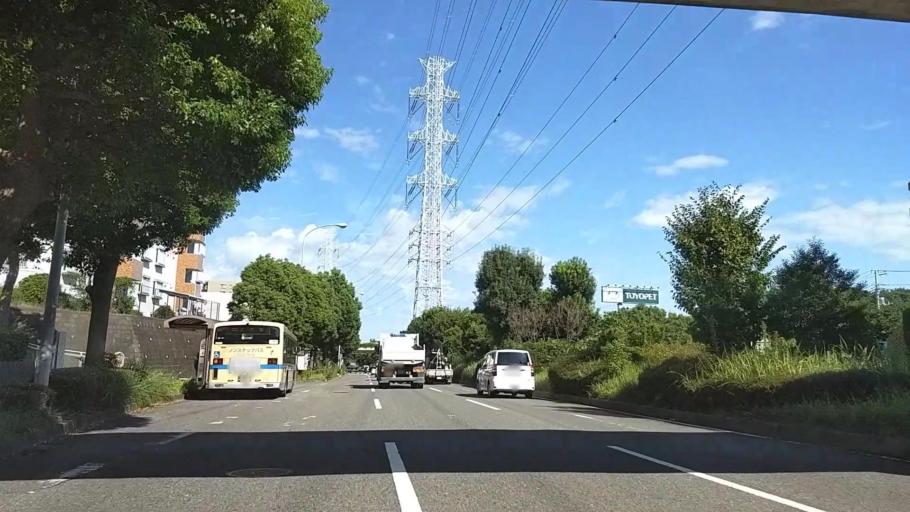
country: JP
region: Tokyo
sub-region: Machida-shi
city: Machida
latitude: 35.5417
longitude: 139.5618
